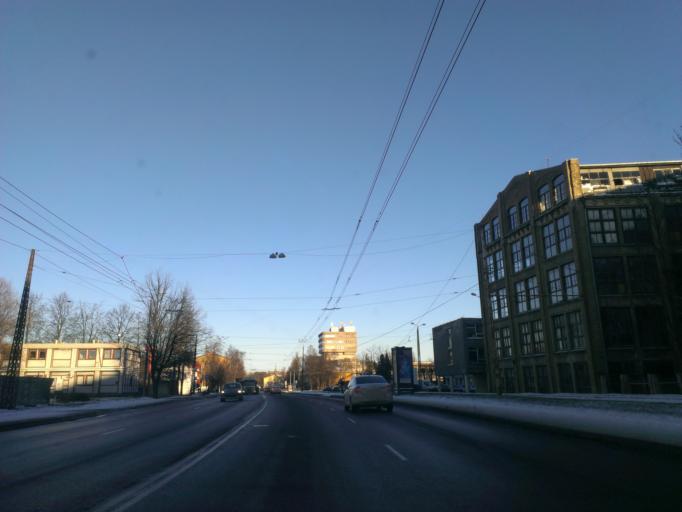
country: LV
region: Riga
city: Riga
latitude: 56.9861
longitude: 24.1210
